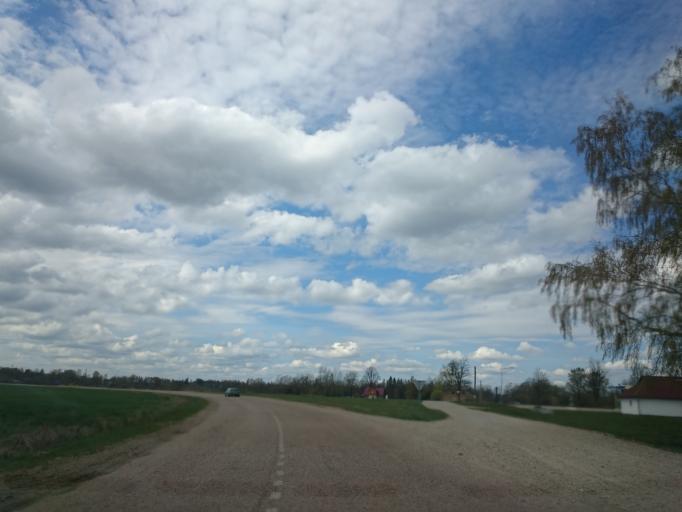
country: LV
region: Talsu Rajons
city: Sabile
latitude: 56.9605
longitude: 22.6206
